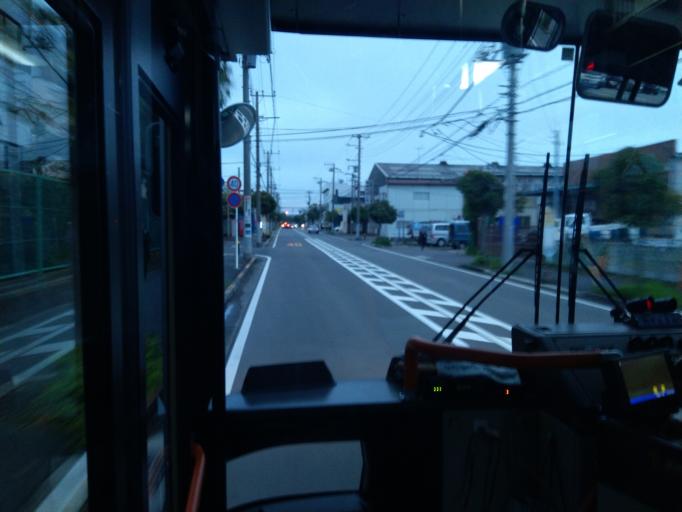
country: JP
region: Kanagawa
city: Hiratsuka
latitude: 35.3362
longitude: 139.3599
